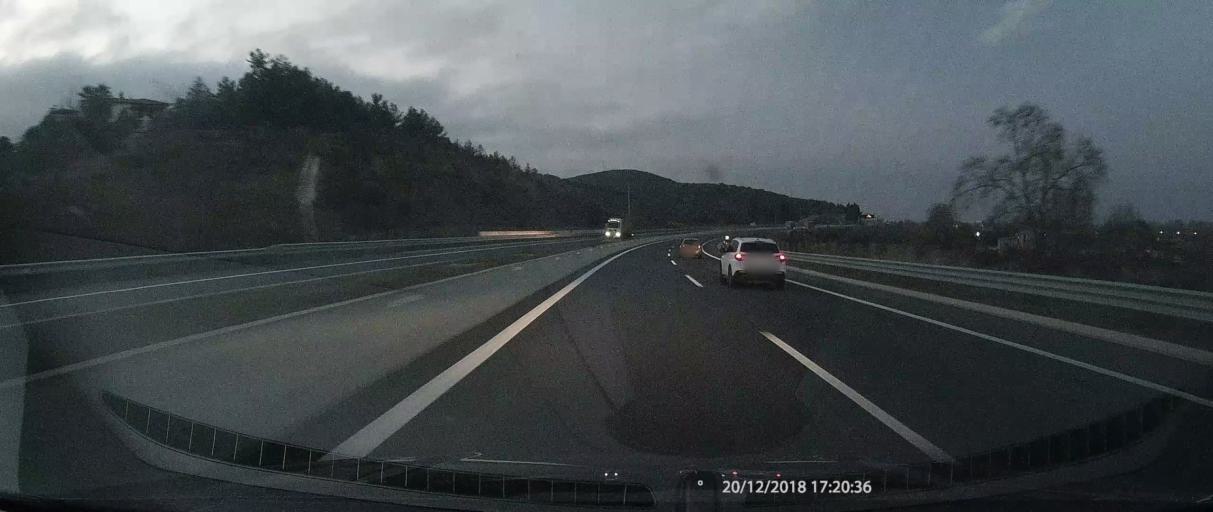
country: GR
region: Thessaly
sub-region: Nomos Larisis
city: Pyrgetos
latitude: 39.9677
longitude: 22.6423
